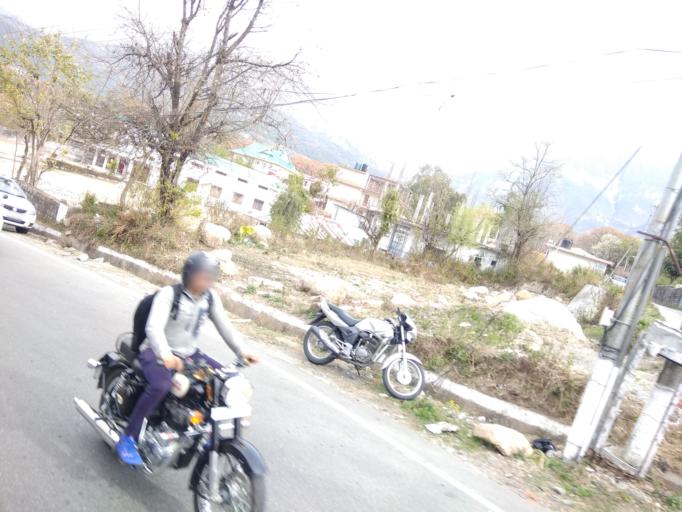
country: IN
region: Himachal Pradesh
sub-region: Kangra
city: Dharmsala
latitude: 32.1954
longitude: 76.3449
